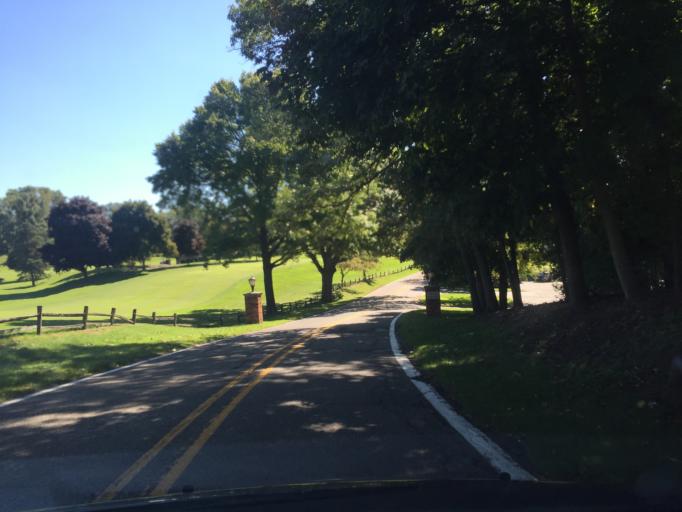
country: US
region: Michigan
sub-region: Oakland County
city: Sylvan Lake
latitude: 42.5988
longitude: -83.2984
